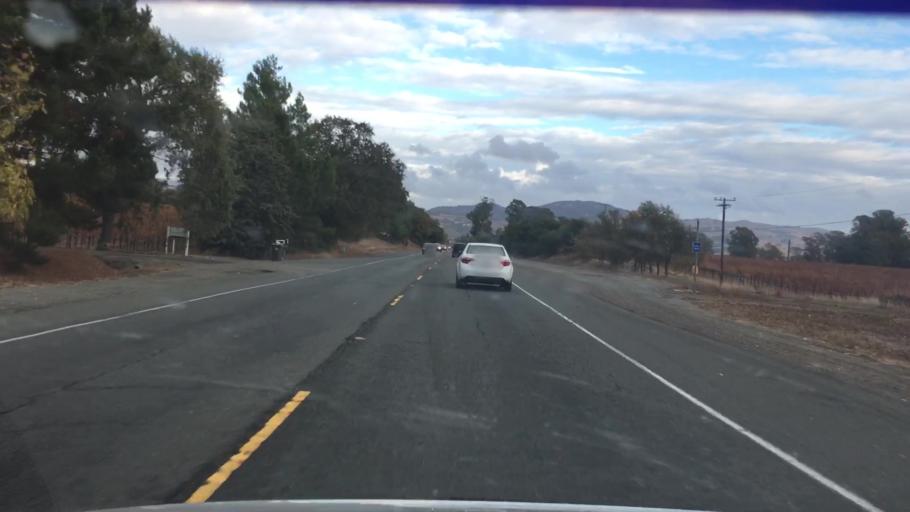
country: US
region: California
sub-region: Napa County
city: Napa
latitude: 38.2576
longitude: -122.3191
